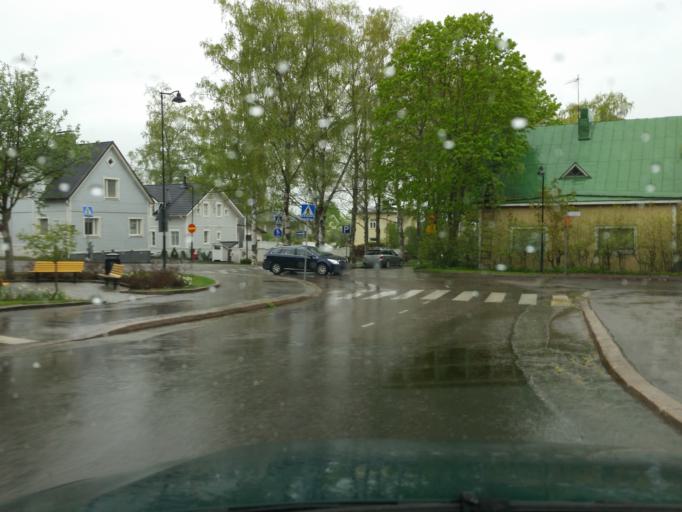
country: FI
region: Uusimaa
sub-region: Helsinki
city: Lohja
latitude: 60.2501
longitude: 24.0593
